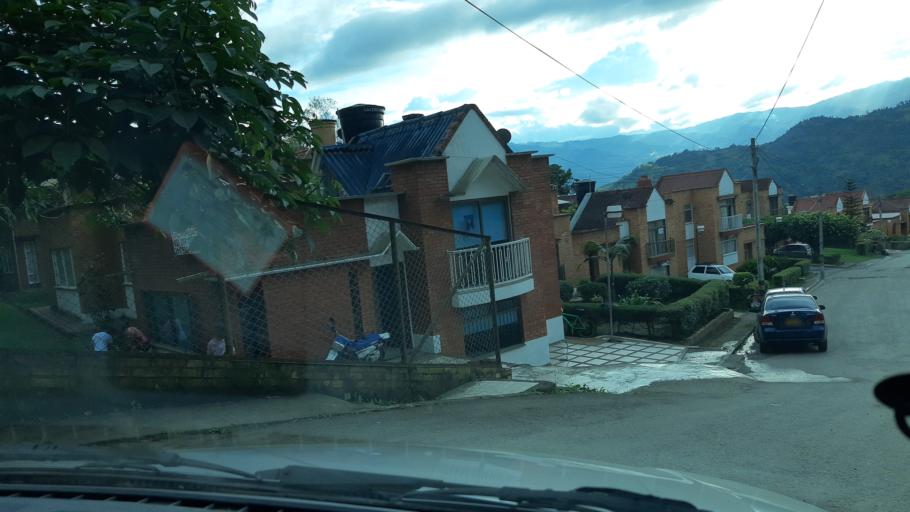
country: CO
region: Boyaca
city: Garagoa
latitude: 5.0882
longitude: -73.3661
